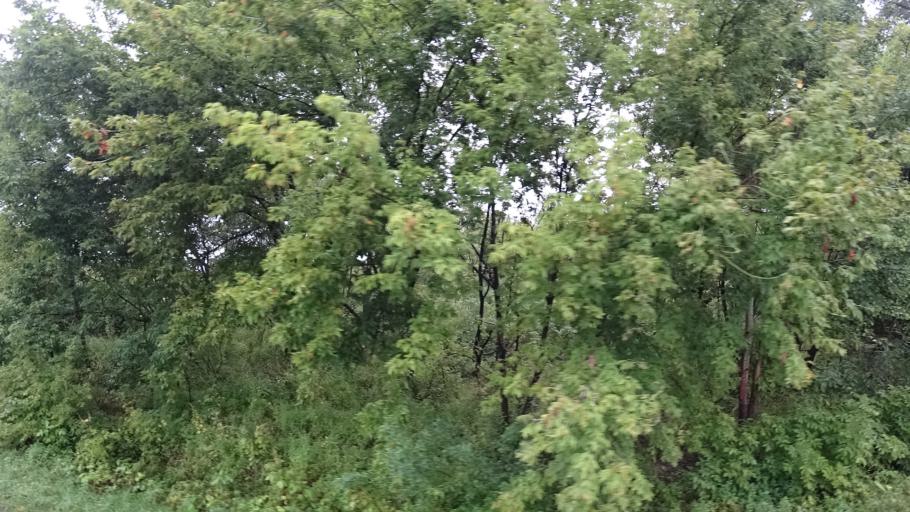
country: RU
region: Primorskiy
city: Monastyrishche
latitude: 44.2678
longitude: 132.4203
